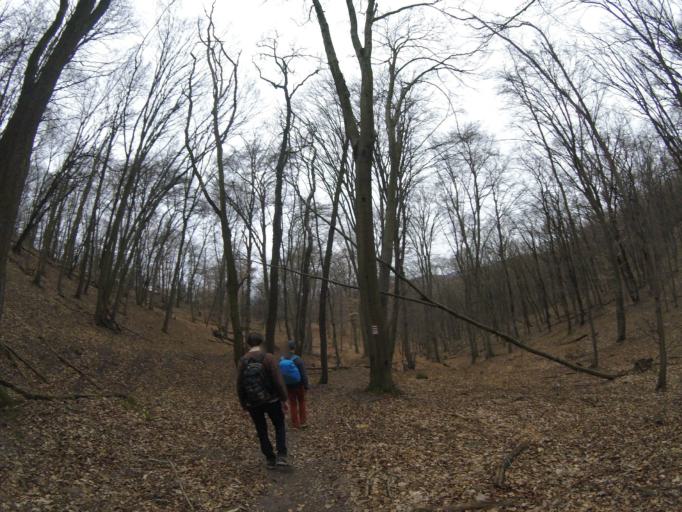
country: HU
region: Pest
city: Szob
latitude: 47.7946
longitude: 18.8215
